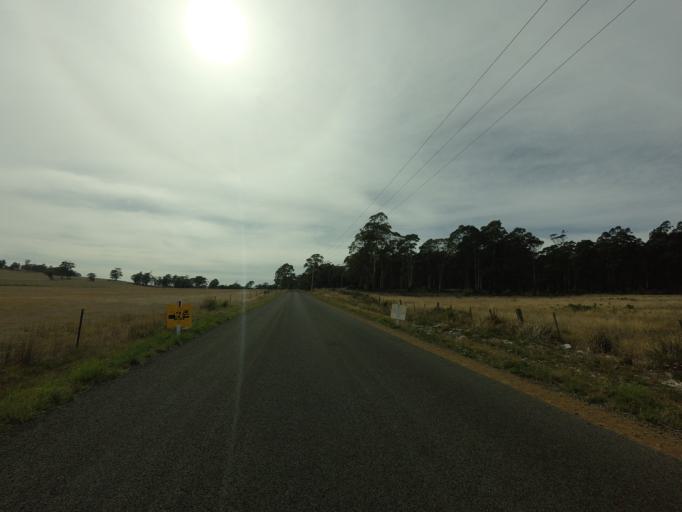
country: AU
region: Tasmania
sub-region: Sorell
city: Sorell
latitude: -42.4263
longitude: 147.4835
